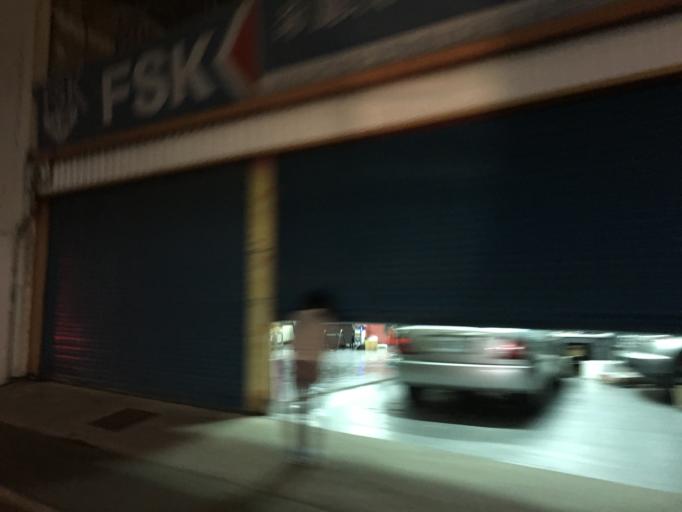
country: TW
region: Taiwan
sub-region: Miaoli
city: Miaoli
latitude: 24.6850
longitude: 120.8856
